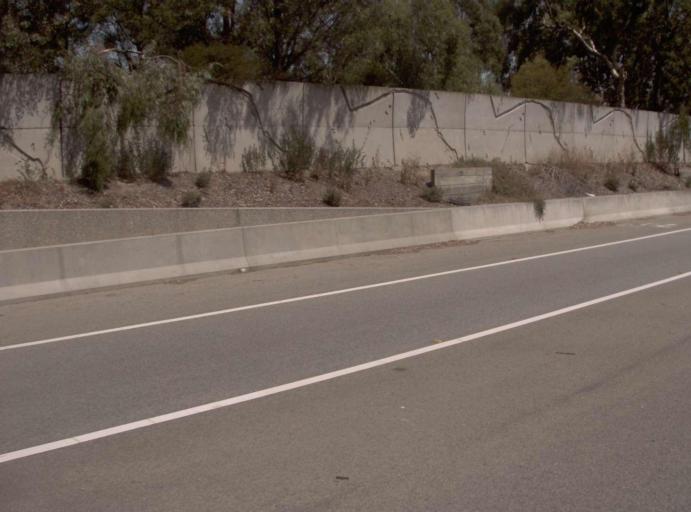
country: AU
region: Victoria
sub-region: Stonnington
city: Glen Iris
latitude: -37.8509
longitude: 145.0500
